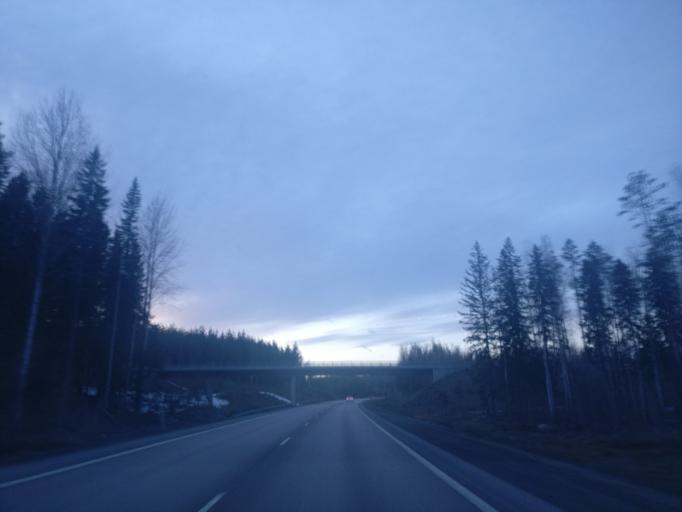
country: FI
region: Central Finland
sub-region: Jyvaeskylae
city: Saeynaetsalo
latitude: 62.1979
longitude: 25.8937
